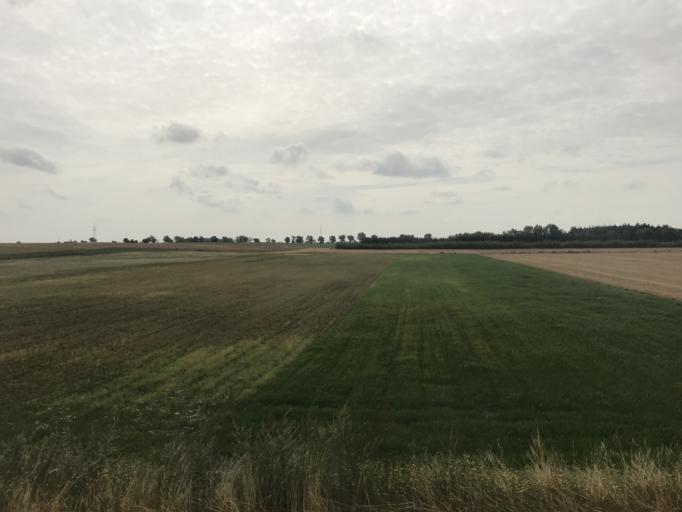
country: PL
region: Kujawsko-Pomorskie
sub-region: Powiat mogilenski
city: Mogilno
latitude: 52.7048
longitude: 18.0198
